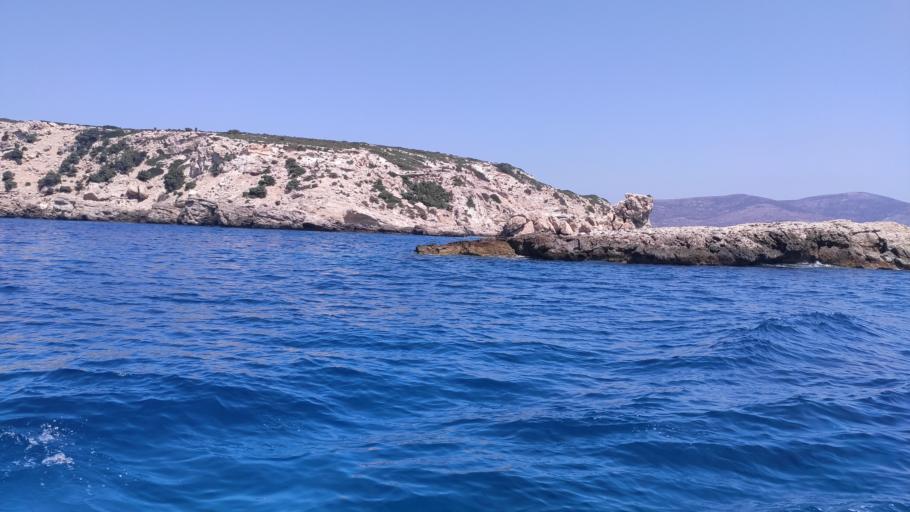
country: GR
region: South Aegean
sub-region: Nomos Dodekanisou
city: Pylion
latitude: 36.9325
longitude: 27.0940
